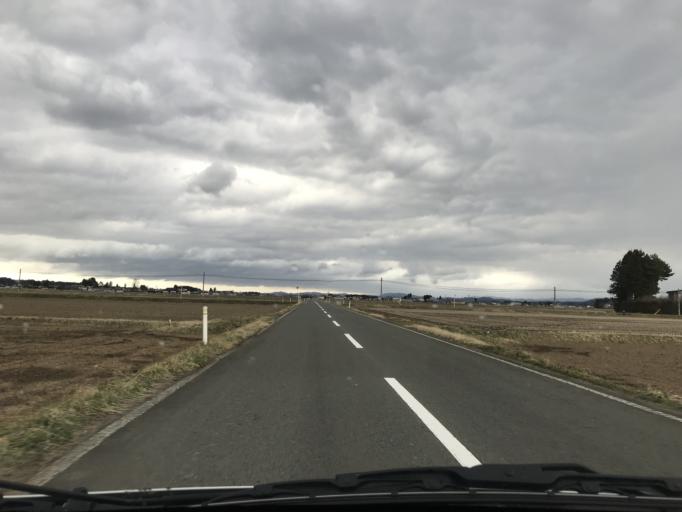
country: JP
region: Iwate
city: Mizusawa
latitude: 39.0920
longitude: 141.1629
